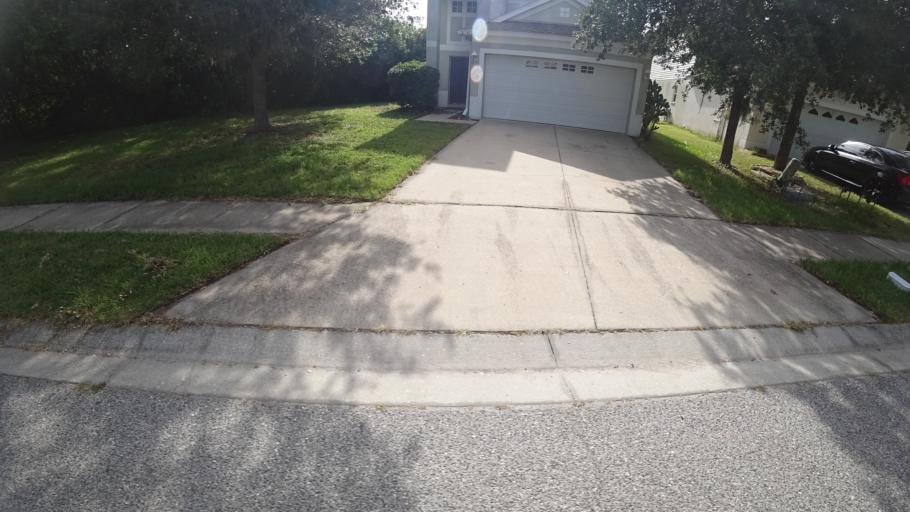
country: US
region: Florida
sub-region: Manatee County
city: Ellenton
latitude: 27.5513
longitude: -82.4967
